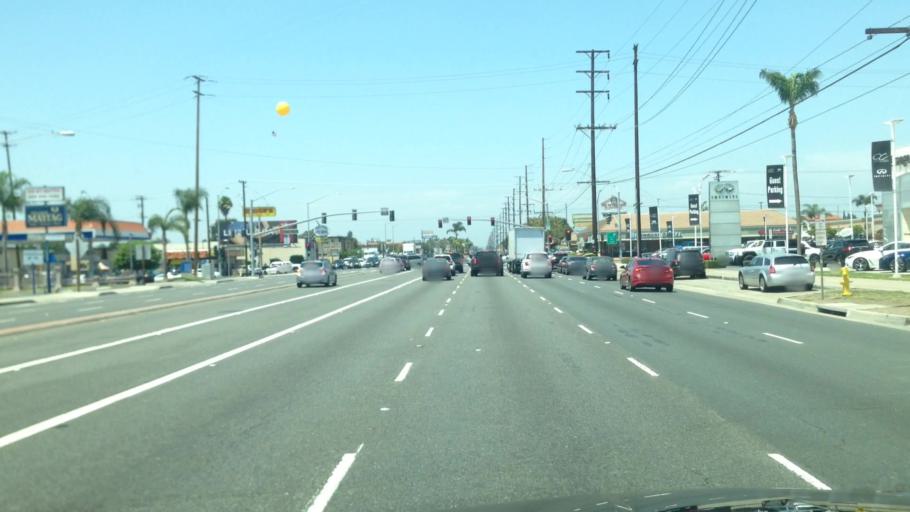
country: US
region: California
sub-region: Orange County
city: Midway City
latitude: 33.7362
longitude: -117.9893
